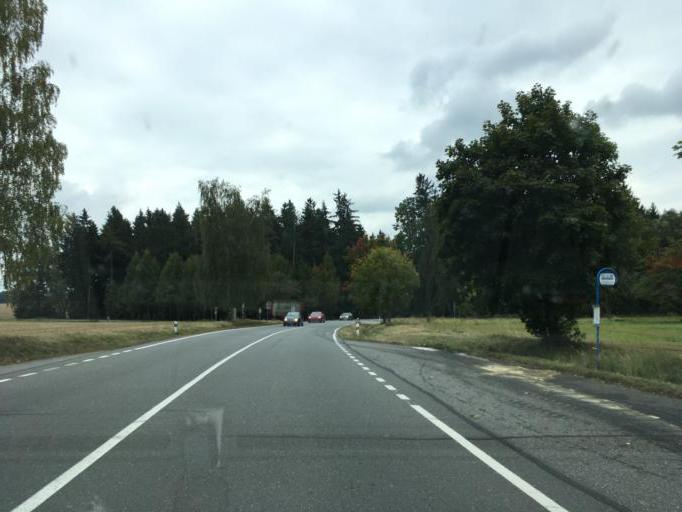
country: CZ
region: Vysocina
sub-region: Okres Pelhrimov
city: Zeliv
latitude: 49.4828
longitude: 15.1806
